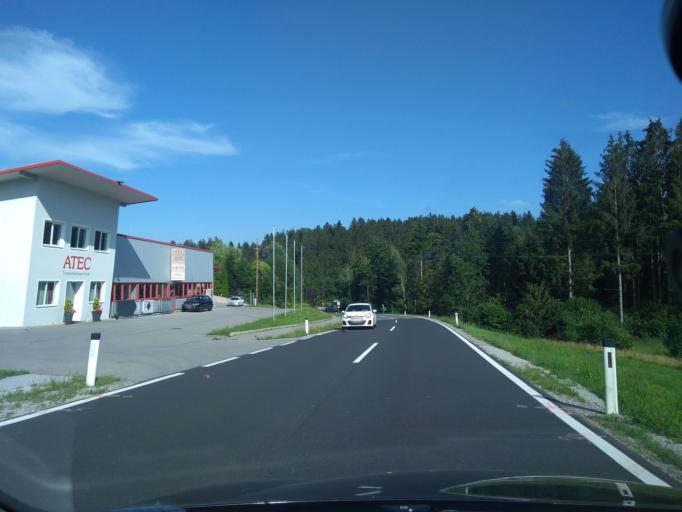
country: AT
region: Styria
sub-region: Politischer Bezirk Graz-Umgebung
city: Semriach
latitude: 47.2691
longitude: 15.4459
